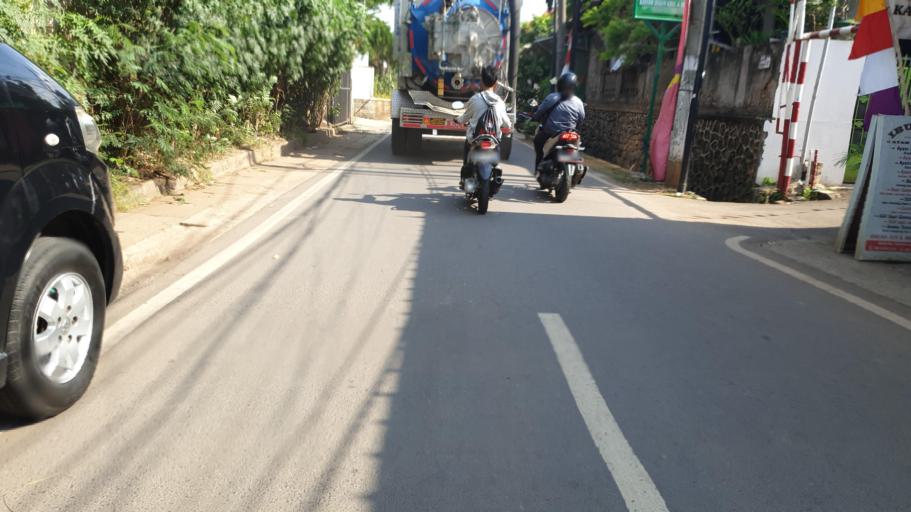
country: ID
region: Jakarta Raya
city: Jakarta
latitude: -6.2886
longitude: 106.8380
